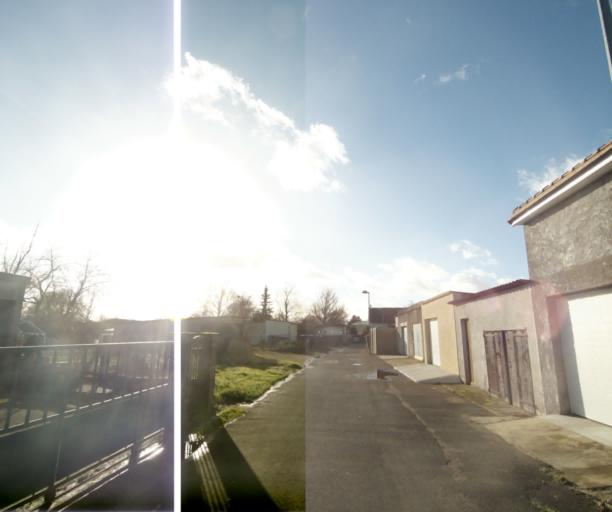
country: FR
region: Pays de la Loire
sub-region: Departement de la Sarthe
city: Le Mans
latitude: 47.9879
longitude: 0.1766
